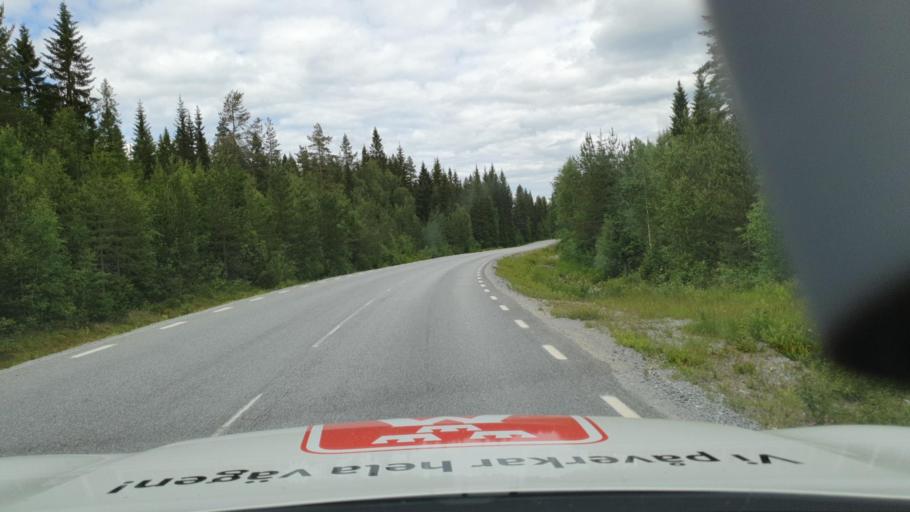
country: SE
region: Vaesterbotten
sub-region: Bjurholms Kommun
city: Bjurholm
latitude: 63.8945
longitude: 19.0651
